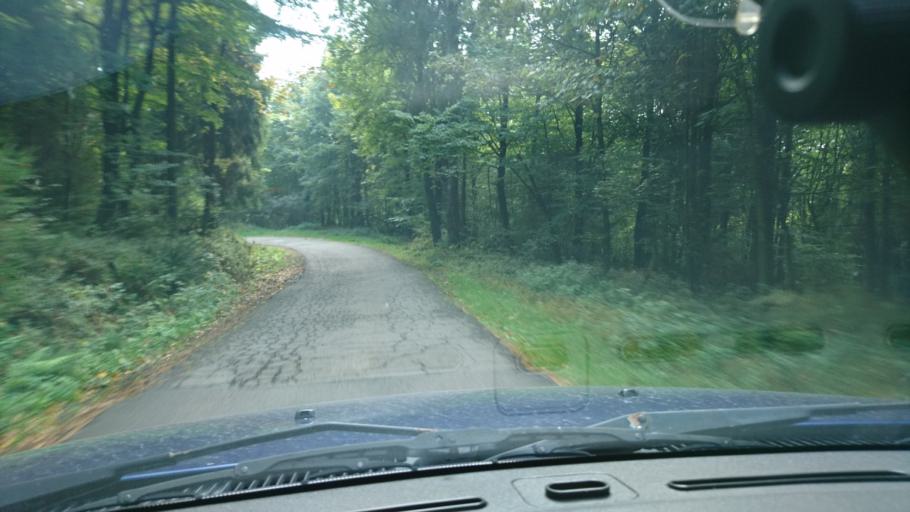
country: PL
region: Silesian Voivodeship
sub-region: Powiat bielski
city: Wilkowice
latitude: 49.7632
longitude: 19.1119
